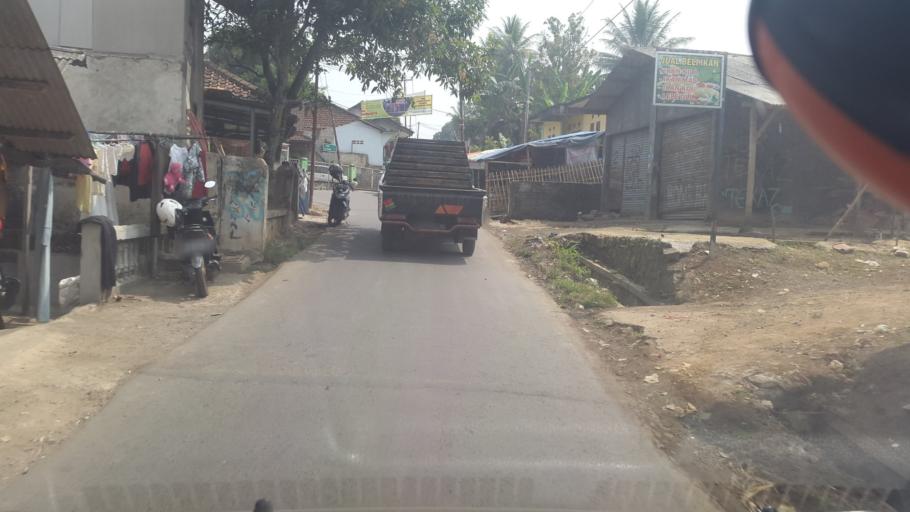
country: ID
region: West Java
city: Sukabumi
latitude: -6.8931
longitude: 106.8667
